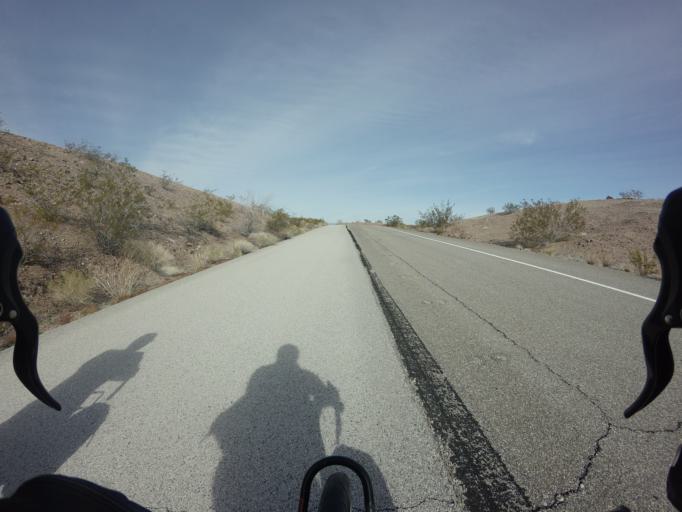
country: US
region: Nevada
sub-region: Clark County
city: Boulder City
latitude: 36.0955
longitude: -114.8435
